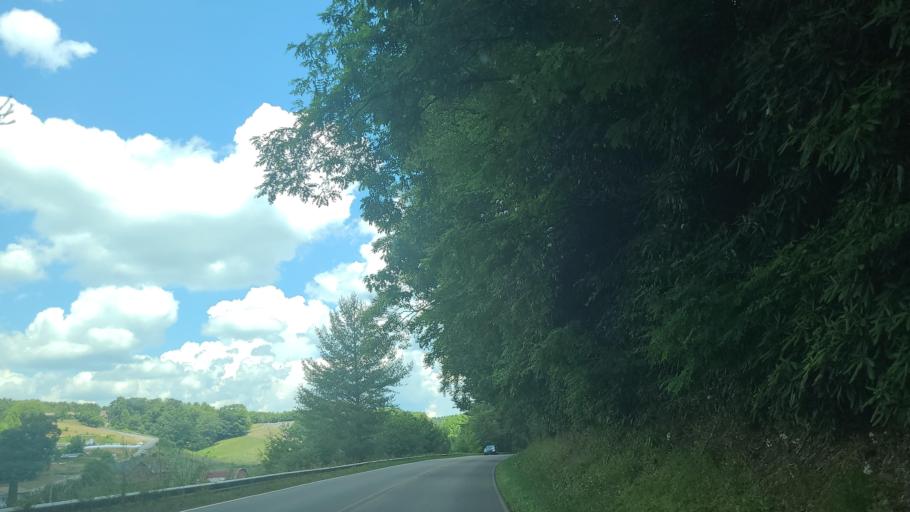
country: US
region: North Carolina
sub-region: Watauga County
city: Boone
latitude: 36.2341
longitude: -81.5548
